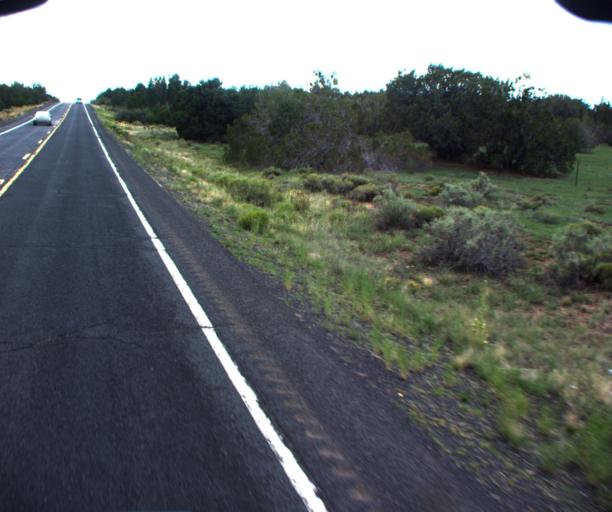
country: US
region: Arizona
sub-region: Coconino County
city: Williams
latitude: 35.4383
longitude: -112.1714
